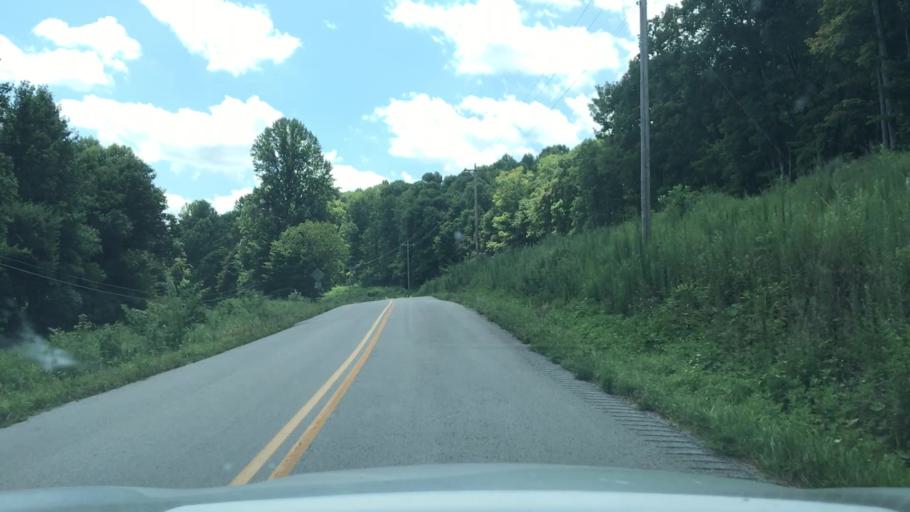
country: US
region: Kentucky
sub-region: Hopkins County
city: Nortonville
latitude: 37.0456
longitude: -87.3473
